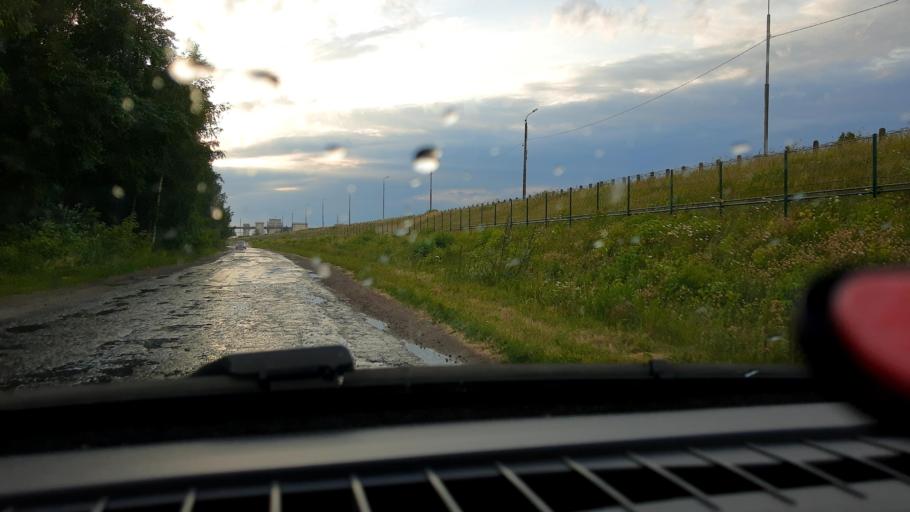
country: RU
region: Nizjnij Novgorod
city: Zavolzh'ye
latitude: 56.6693
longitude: 43.4282
